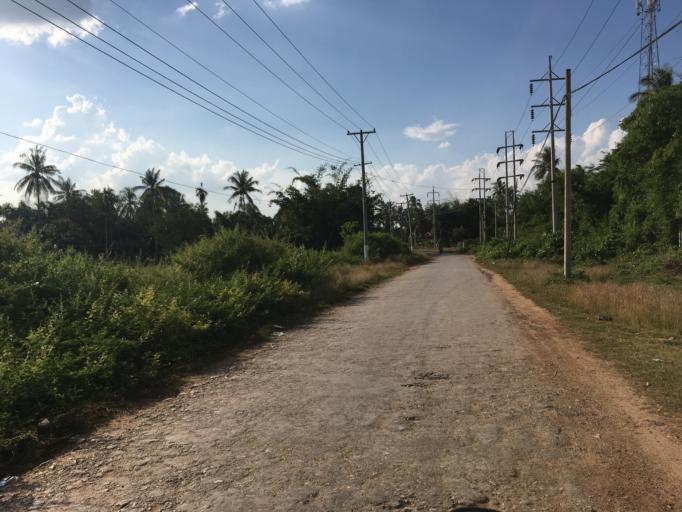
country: MM
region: Mon
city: Mawlamyine
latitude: 16.4276
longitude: 97.6313
